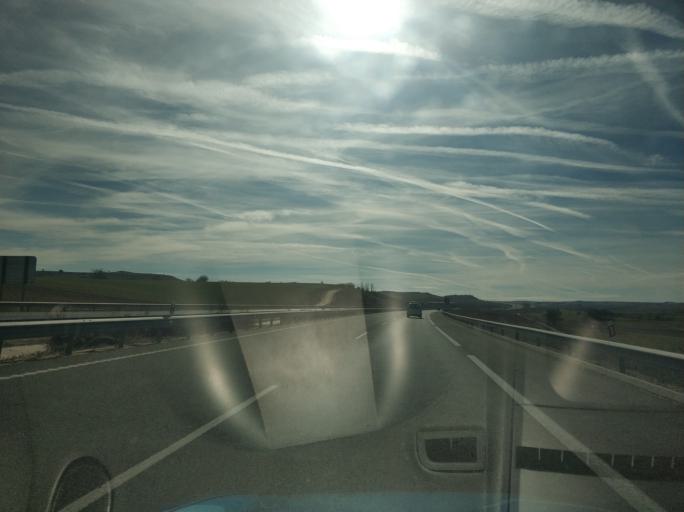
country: ES
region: Castille and Leon
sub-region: Provincia de Zamora
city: Corrales
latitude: 41.3505
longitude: -5.7147
